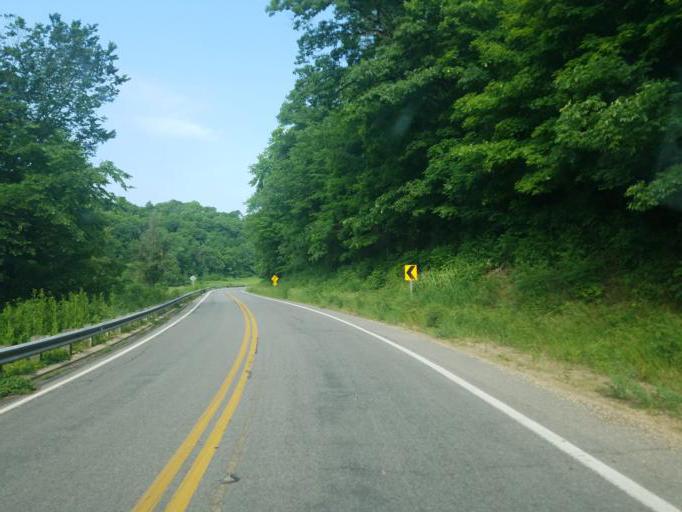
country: US
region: Wisconsin
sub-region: Vernon County
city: Hillsboro
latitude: 43.6746
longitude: -90.4808
